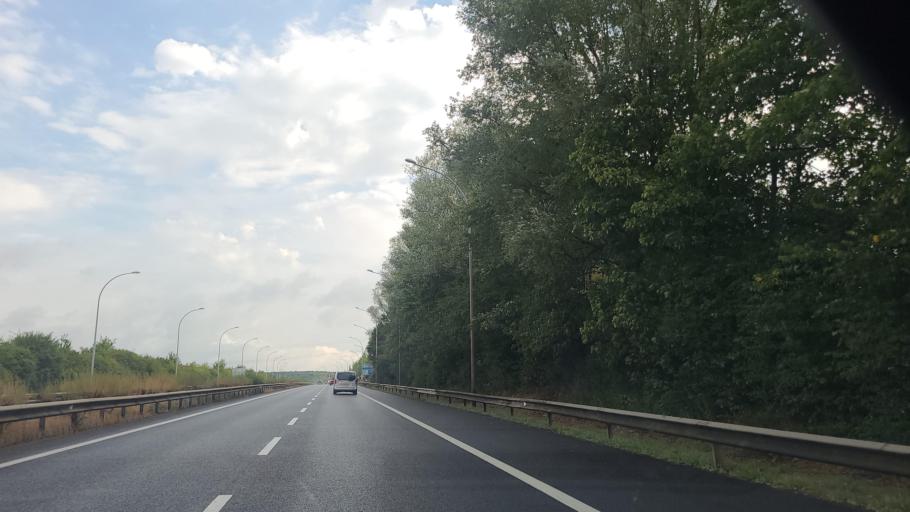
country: LU
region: Luxembourg
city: Pontpierre
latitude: 49.5430
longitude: 6.0353
